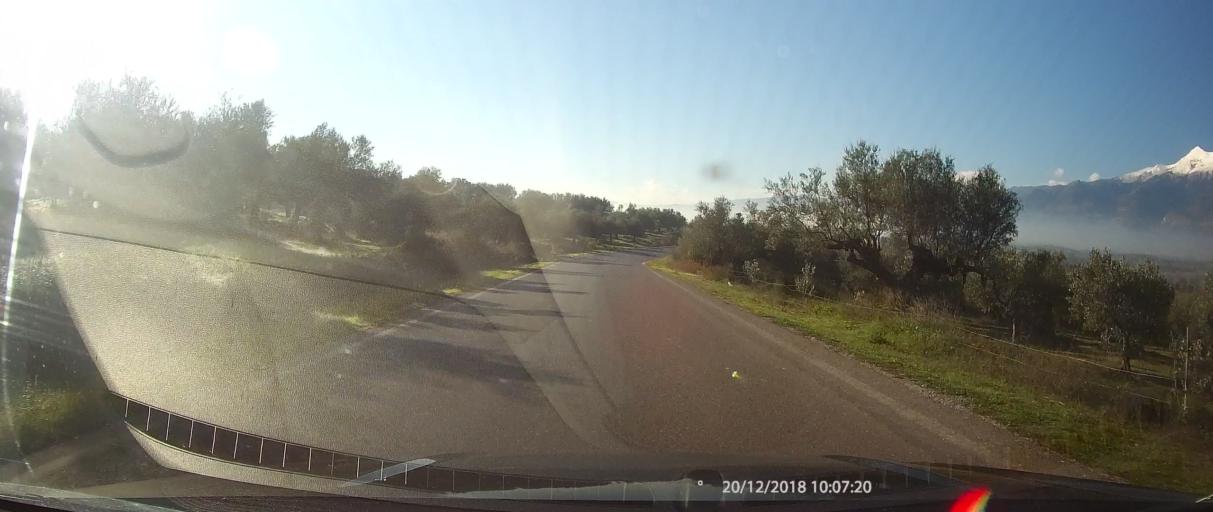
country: GR
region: Peloponnese
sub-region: Nomos Lakonias
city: Sparti
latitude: 37.0205
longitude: 22.4962
